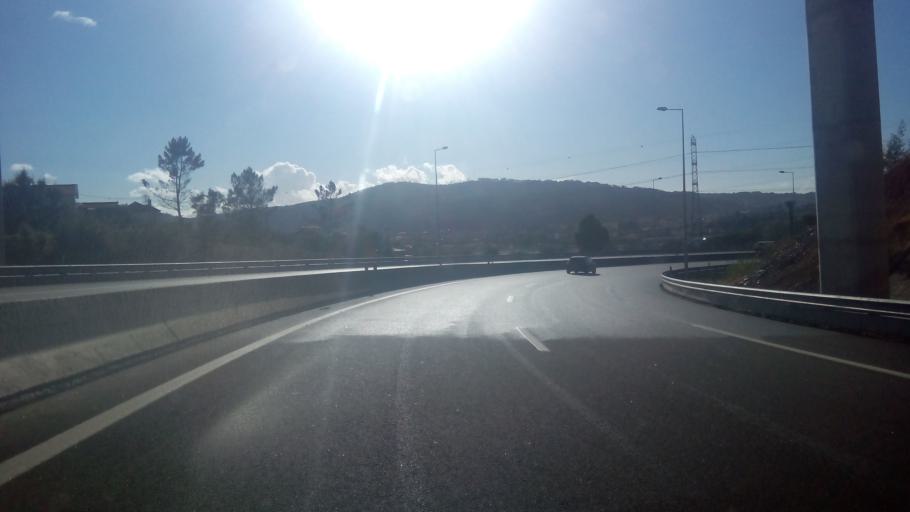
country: PT
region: Porto
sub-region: Valongo
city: Campo
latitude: 41.1819
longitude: -8.4525
